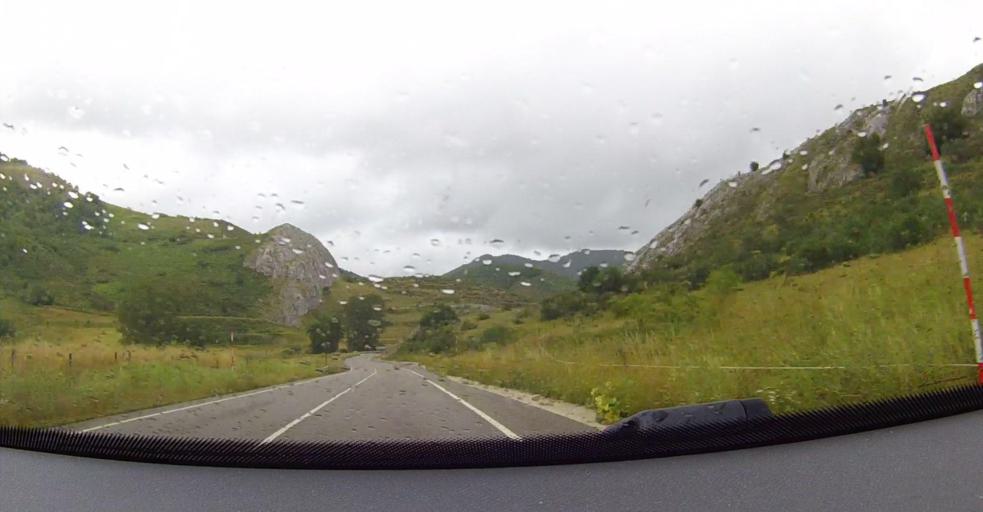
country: ES
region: Castille and Leon
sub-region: Provincia de Leon
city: Marana
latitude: 43.0700
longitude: -5.1449
